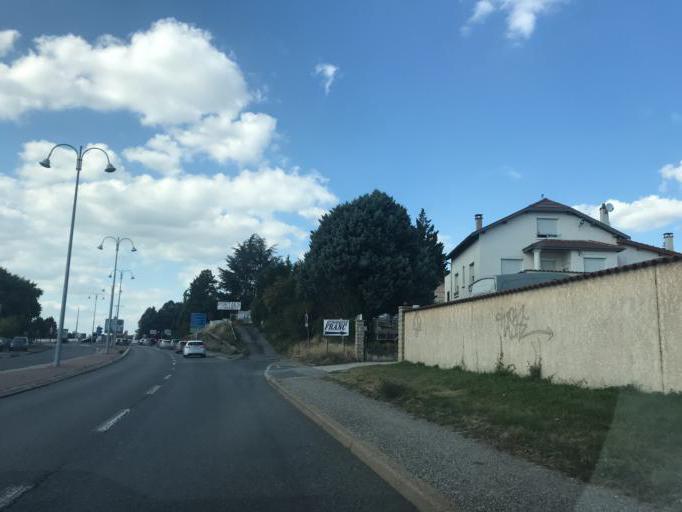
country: FR
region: Rhone-Alpes
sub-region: Departement du Rhone
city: Limonest
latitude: 45.8227
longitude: 4.7659
